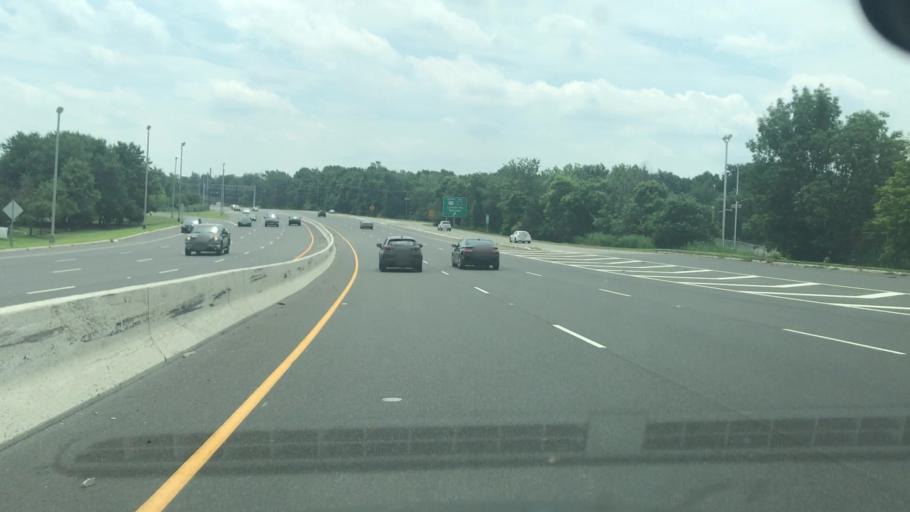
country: US
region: New Jersey
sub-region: Passaic County
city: Wayne
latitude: 40.9138
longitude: -74.2653
